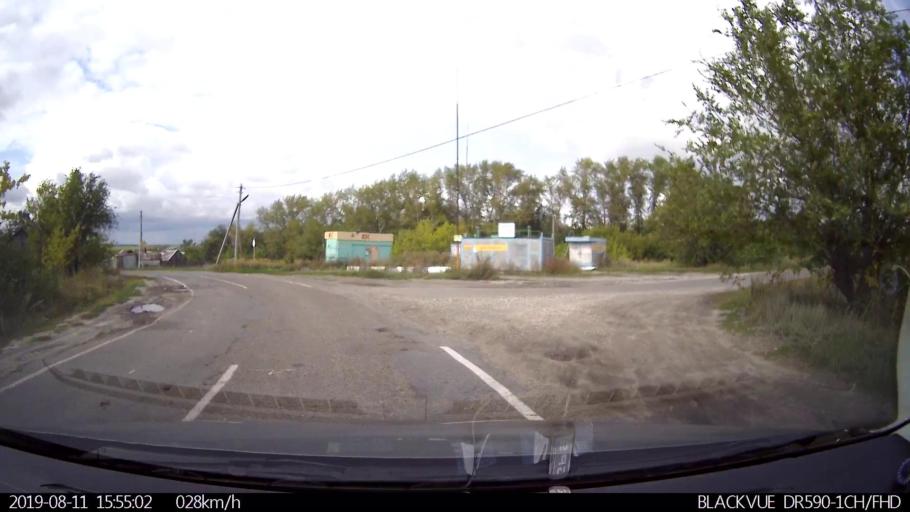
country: RU
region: Ulyanovsk
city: Ignatovka
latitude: 53.9442
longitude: 47.6561
